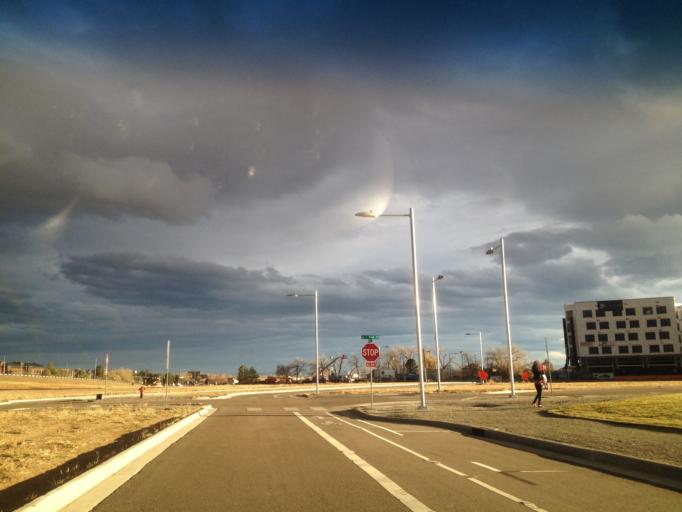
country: US
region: Colorado
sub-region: Adams County
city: Westminster
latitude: 39.8601
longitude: -105.0586
